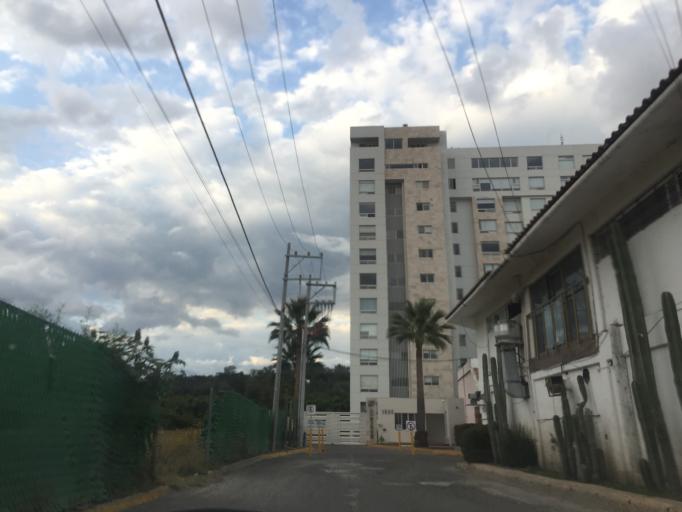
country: MX
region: Guanajuato
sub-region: Leon
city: La Ermita
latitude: 21.1692
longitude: -101.6934
